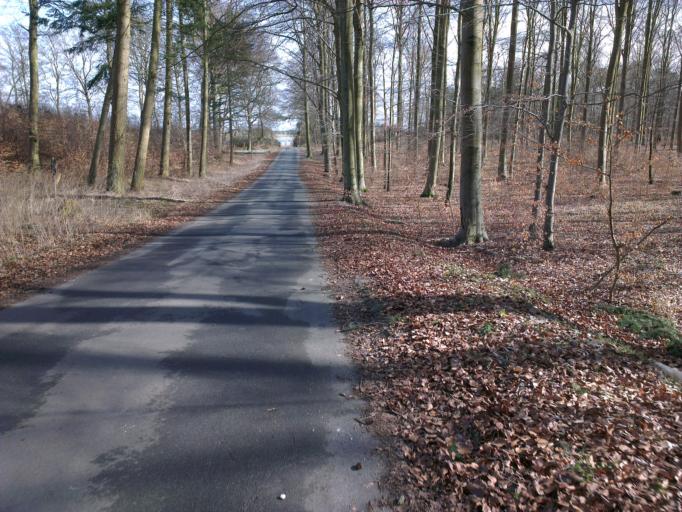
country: DK
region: Zealand
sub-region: Roskilde Kommune
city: Jyllinge
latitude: 55.7351
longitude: 12.0594
